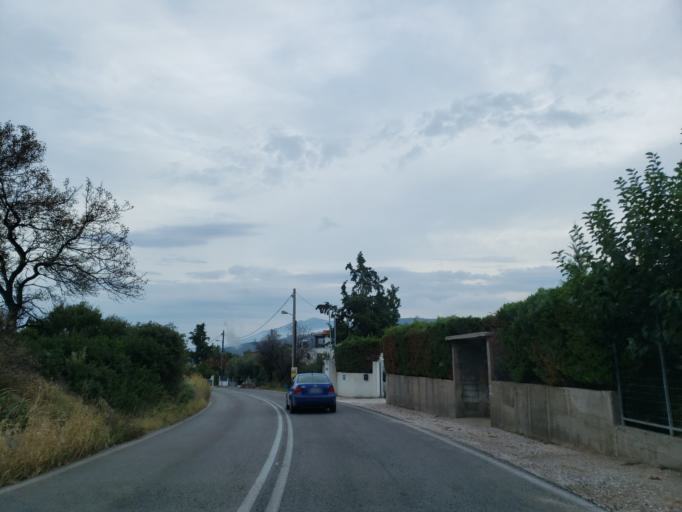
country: GR
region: Attica
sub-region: Nomarchia Anatolikis Attikis
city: Marathonas
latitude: 38.1645
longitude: 23.9623
